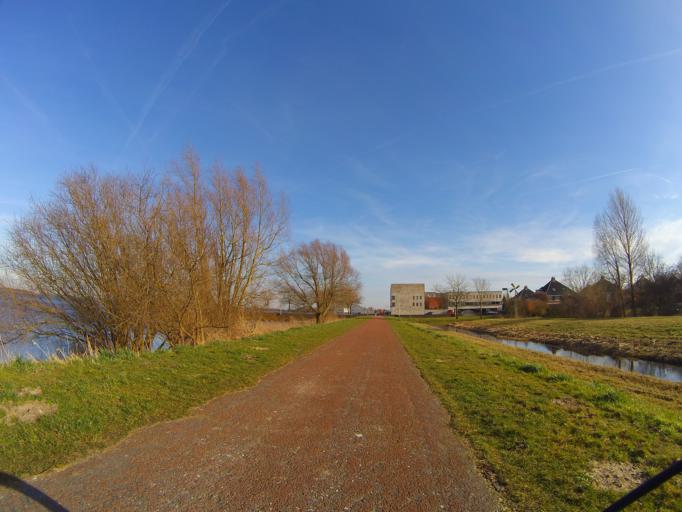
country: NL
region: North Holland
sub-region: Gemeente Huizen
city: Huizen
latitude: 52.3028
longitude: 5.2769
